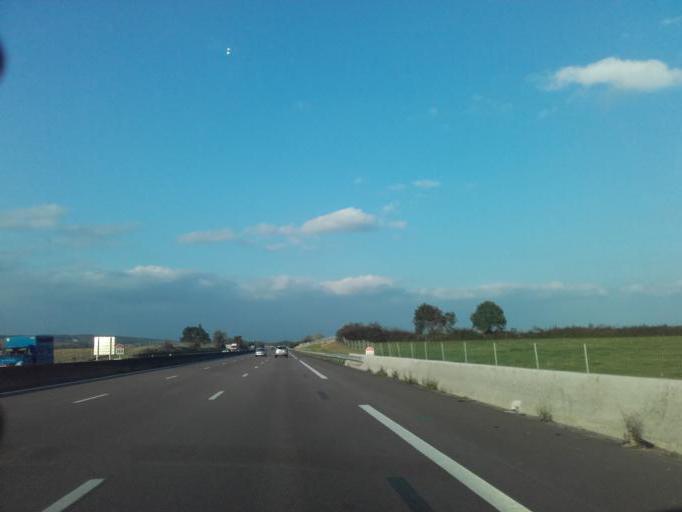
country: FR
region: Rhone-Alpes
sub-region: Departement de l'Ain
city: Pont-de-Vaux
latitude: 46.4776
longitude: 4.8877
